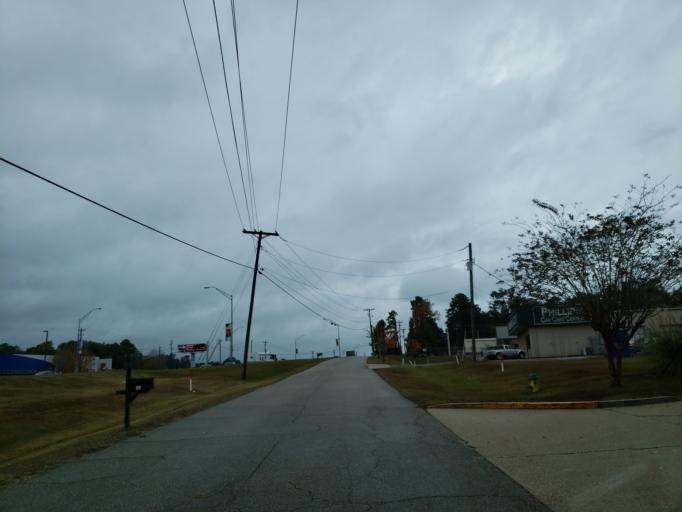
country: US
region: Mississippi
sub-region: Forrest County
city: Rawls Springs
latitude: 31.3632
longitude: -89.3519
